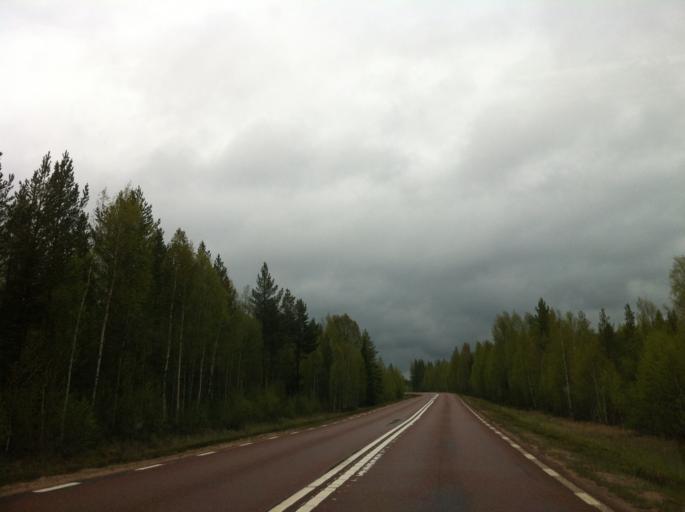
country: SE
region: Jaemtland
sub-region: Harjedalens Kommun
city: Sveg
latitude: 61.8930
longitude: 14.6220
